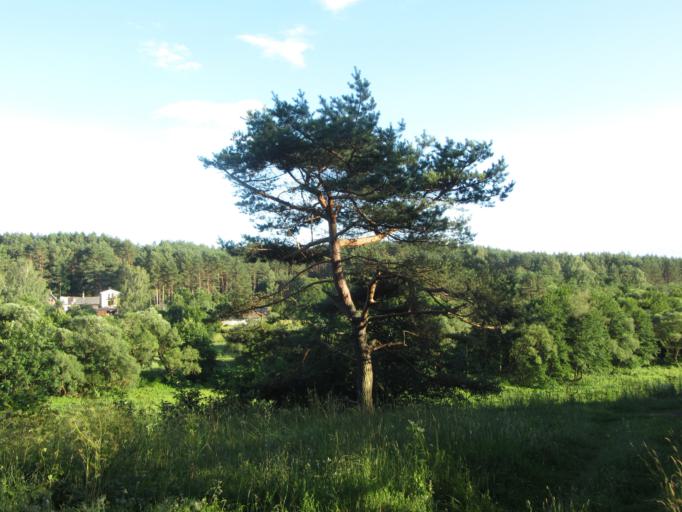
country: LT
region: Vilnius County
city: Rasos
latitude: 54.7507
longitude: 25.3208
